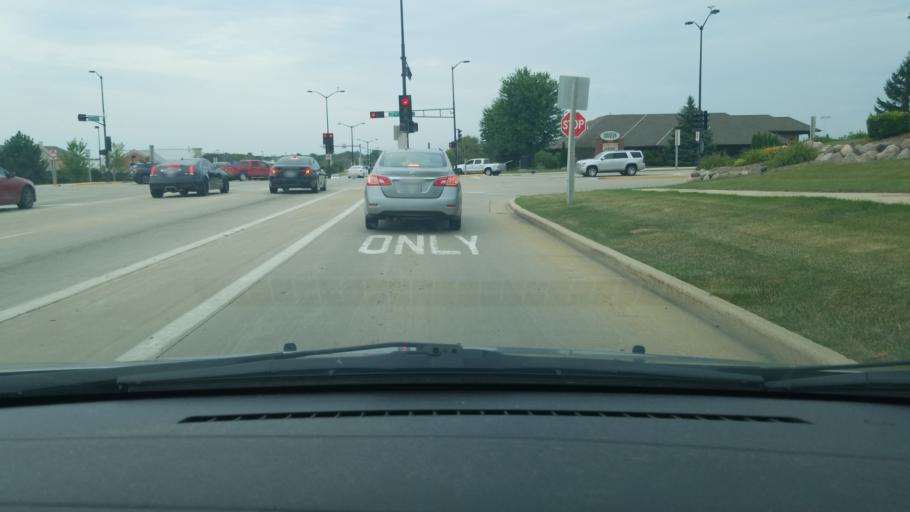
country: US
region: Wisconsin
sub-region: Ozaukee County
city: Grafton
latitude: 43.3202
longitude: -87.9259
